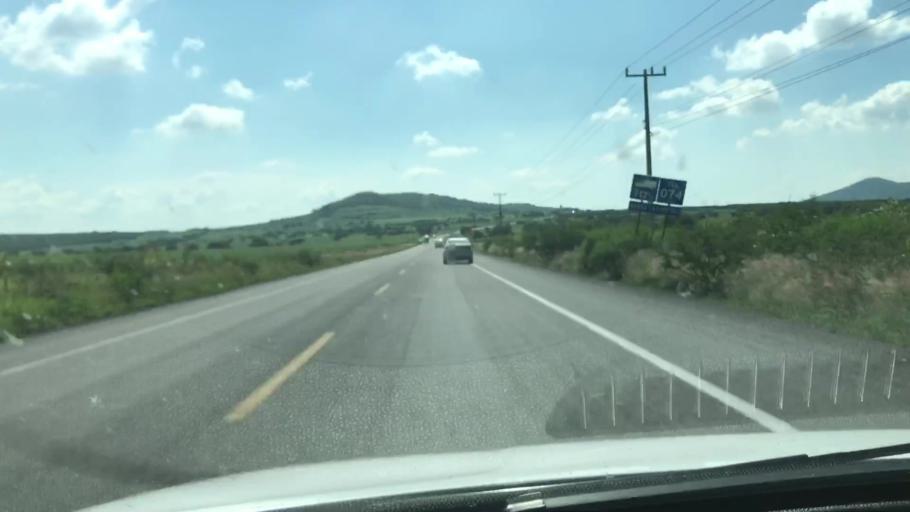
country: MX
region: Michoacan
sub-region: Yurecuaro
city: Yurecuaro
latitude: 20.3417
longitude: -102.1869
